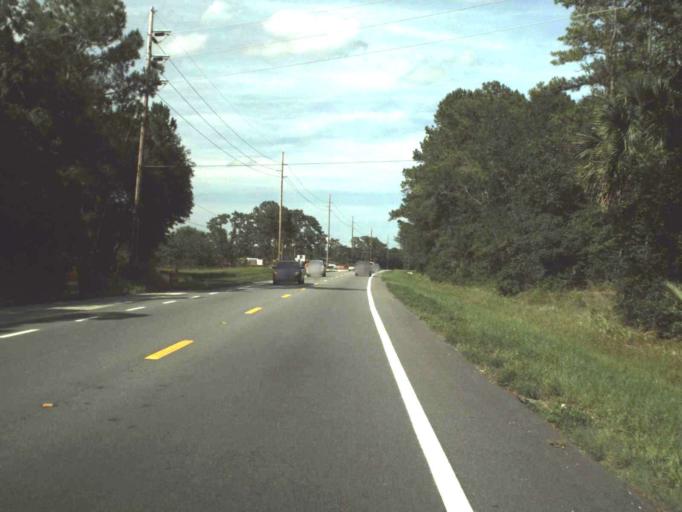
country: US
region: Florida
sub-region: Volusia County
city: West DeLand
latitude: 29.0170
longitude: -81.3724
